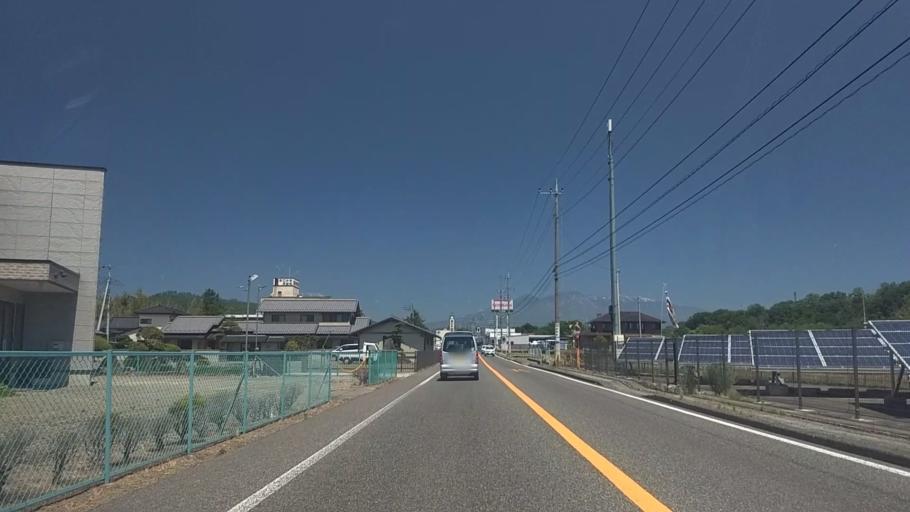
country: JP
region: Yamanashi
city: Nirasaki
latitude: 35.7431
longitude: 138.4419
